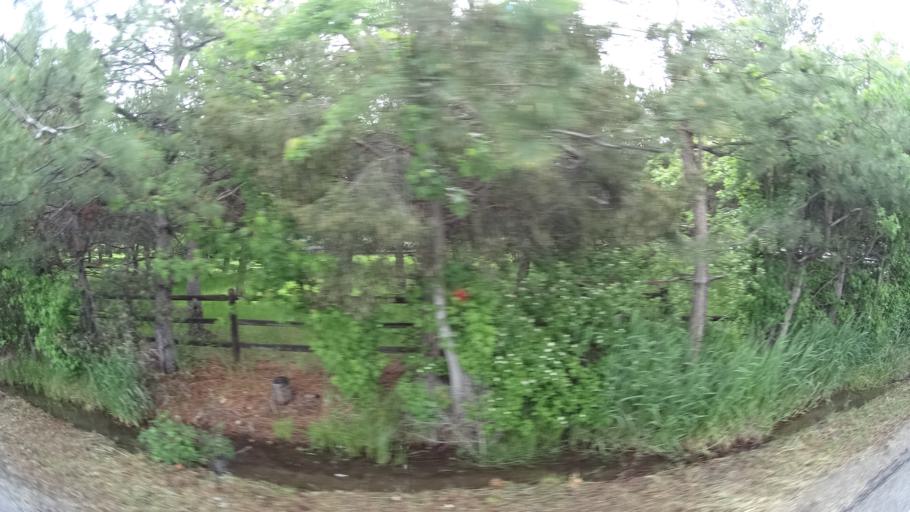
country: US
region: Idaho
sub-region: Ada County
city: Eagle
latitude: 43.7113
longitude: -116.3539
